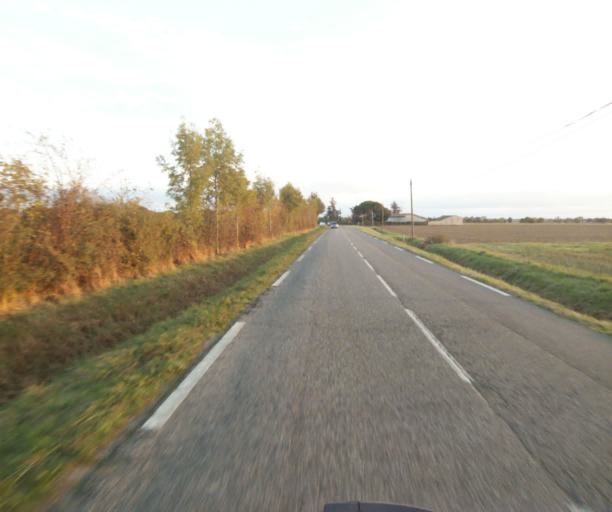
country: FR
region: Midi-Pyrenees
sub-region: Departement du Tarn-et-Garonne
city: Verdun-sur-Garonne
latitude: 43.8336
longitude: 1.2407
